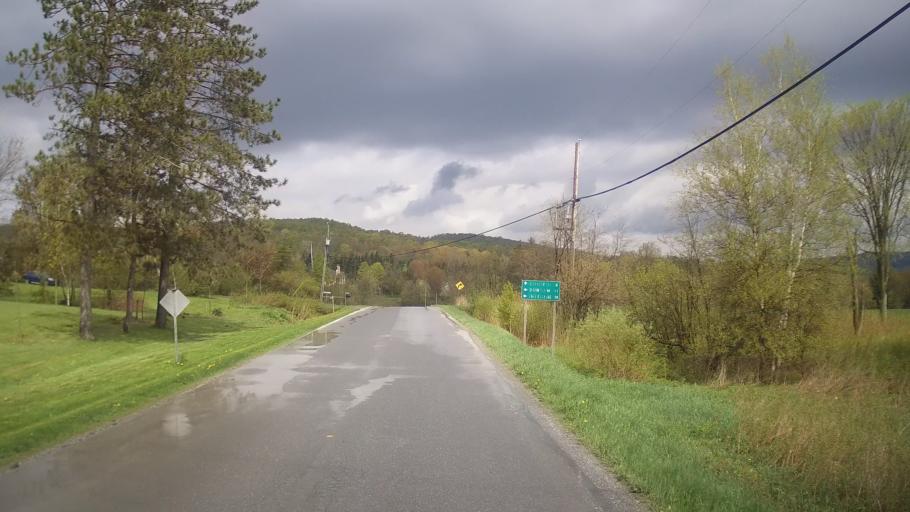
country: CA
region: Quebec
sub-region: Monteregie
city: Cowansville
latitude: 45.1756
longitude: -72.6905
